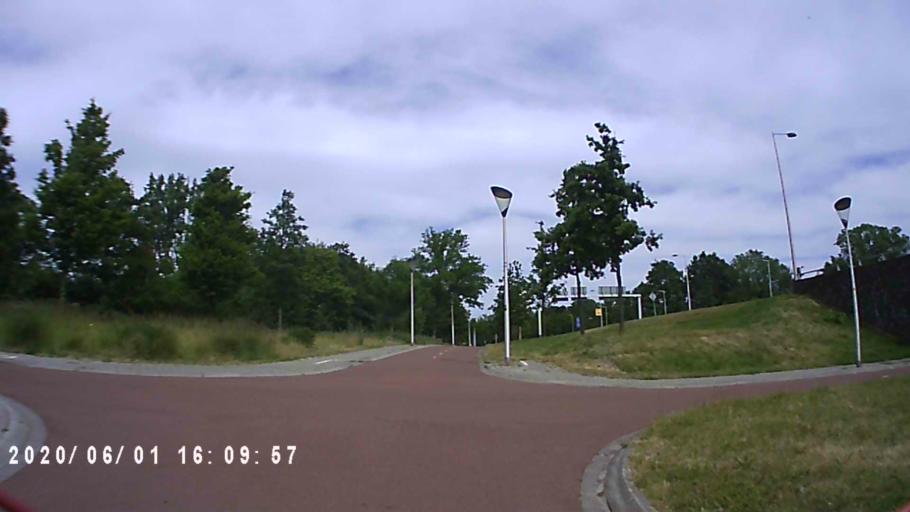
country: NL
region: Friesland
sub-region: Gemeente Leeuwarden
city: Huizum
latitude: 53.1901
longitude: 5.8170
